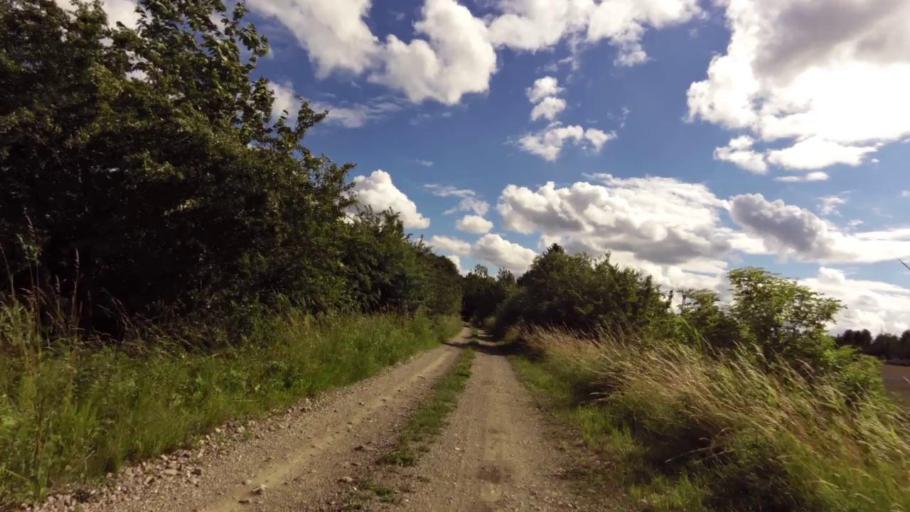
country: PL
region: West Pomeranian Voivodeship
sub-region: Powiat slawienski
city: Slawno
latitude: 54.5083
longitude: 16.7045
